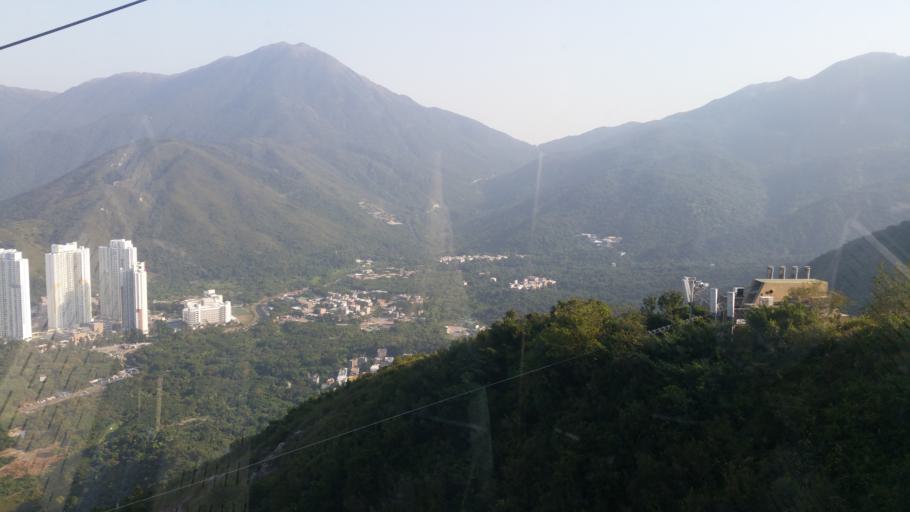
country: HK
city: Tai O
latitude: 22.2819
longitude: 113.9219
